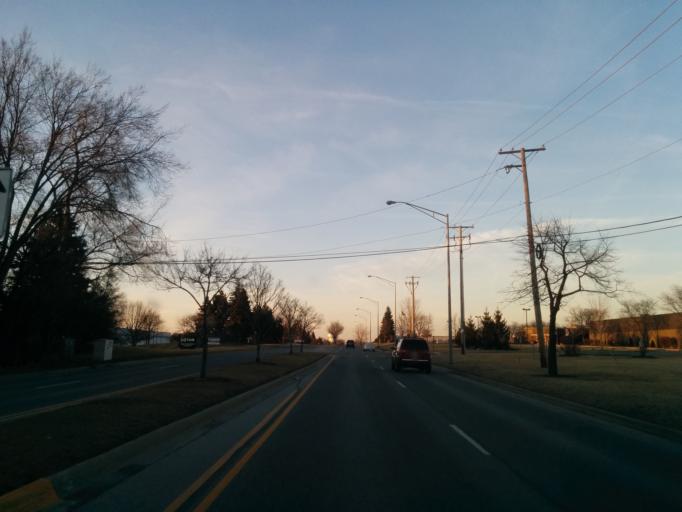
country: US
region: Illinois
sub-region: DuPage County
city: Glendale Heights
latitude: 41.9234
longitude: -88.0423
